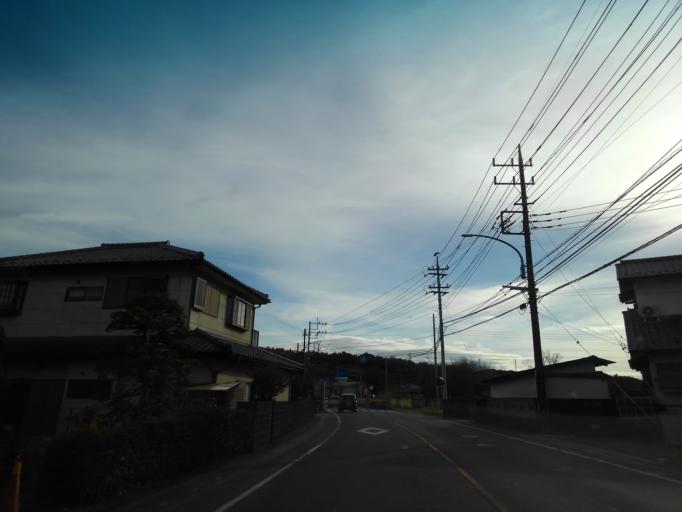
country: JP
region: Saitama
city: Hanno
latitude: 35.8885
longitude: 139.3388
